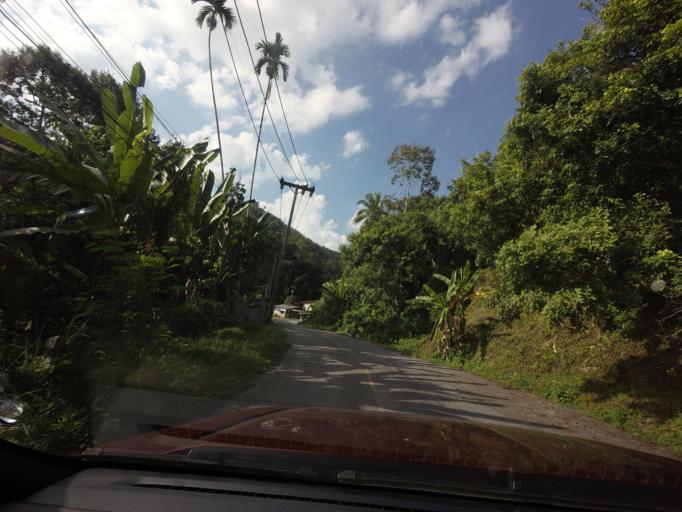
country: TH
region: Yala
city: Than To
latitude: 6.1402
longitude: 101.2976
